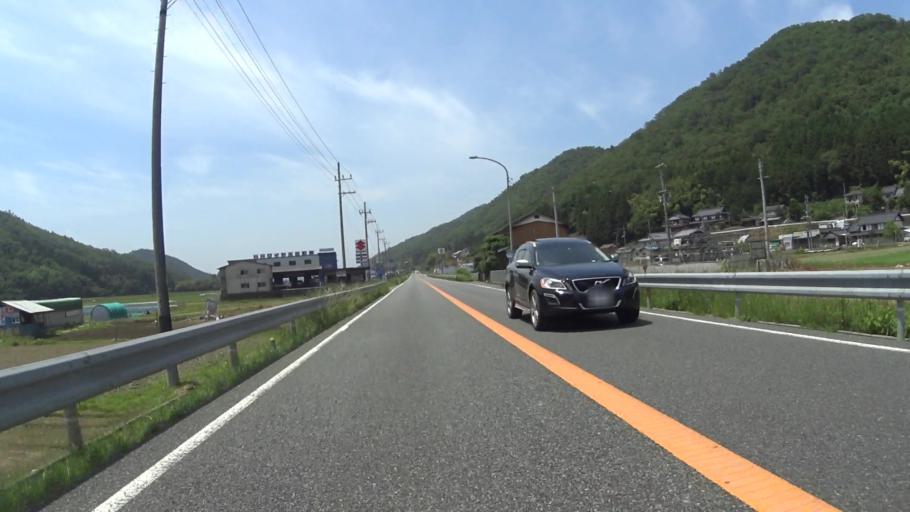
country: JP
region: Kyoto
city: Ayabe
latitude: 35.2548
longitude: 135.2041
